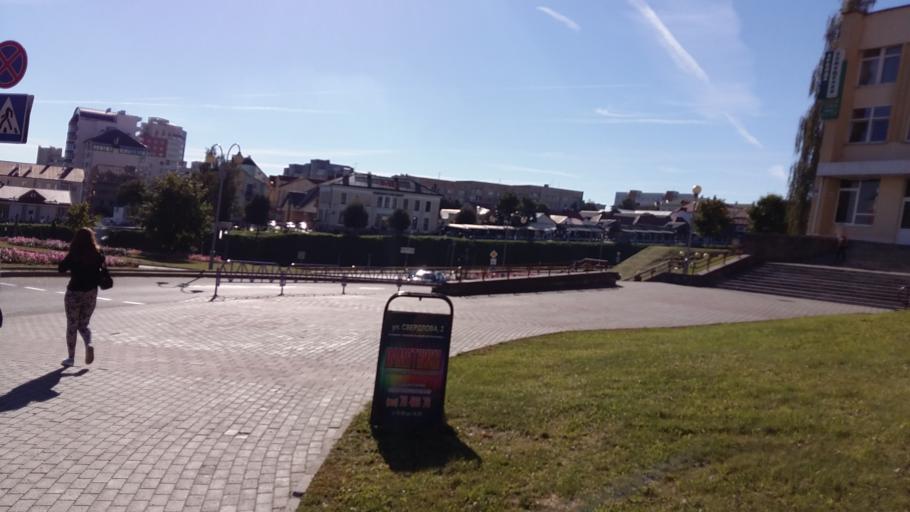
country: BY
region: Grodnenskaya
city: Hrodna
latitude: 53.6768
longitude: 23.8387
